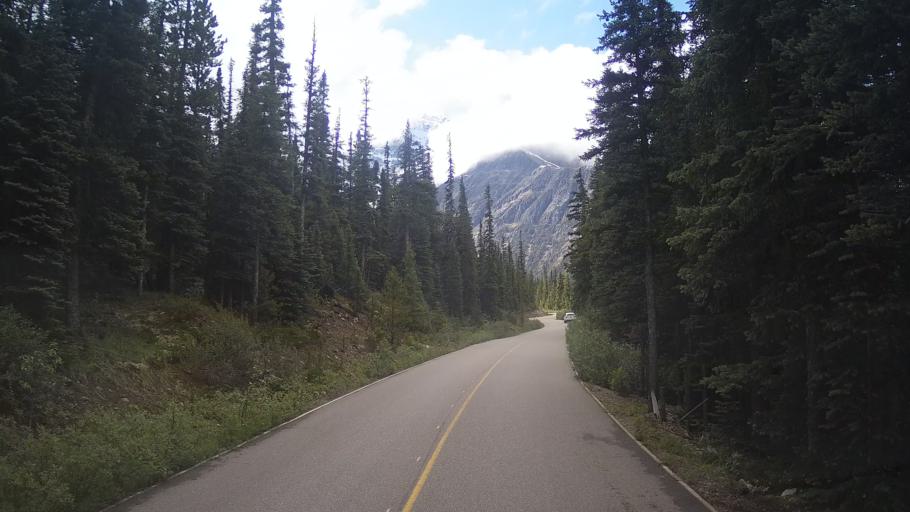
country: CA
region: Alberta
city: Jasper Park Lodge
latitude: 52.7129
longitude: -118.0553
